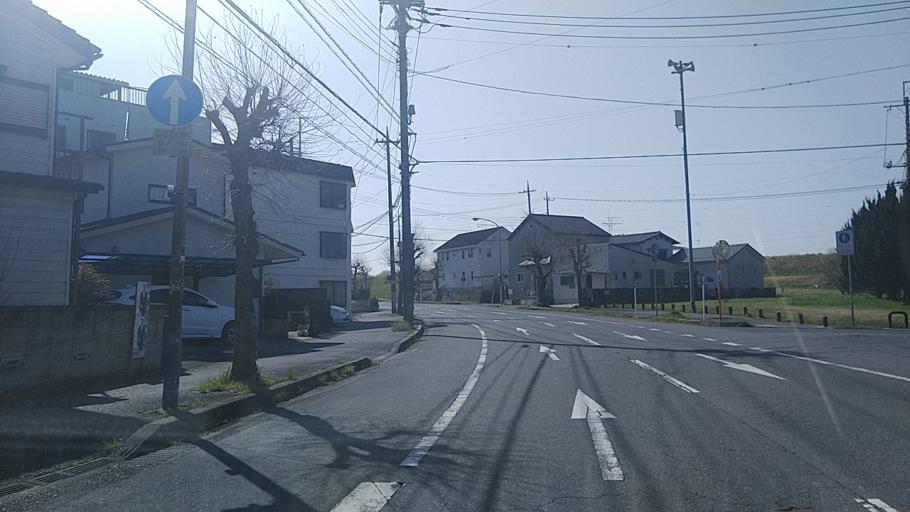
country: JP
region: Ibaraki
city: Toride
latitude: 35.8979
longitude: 140.0550
